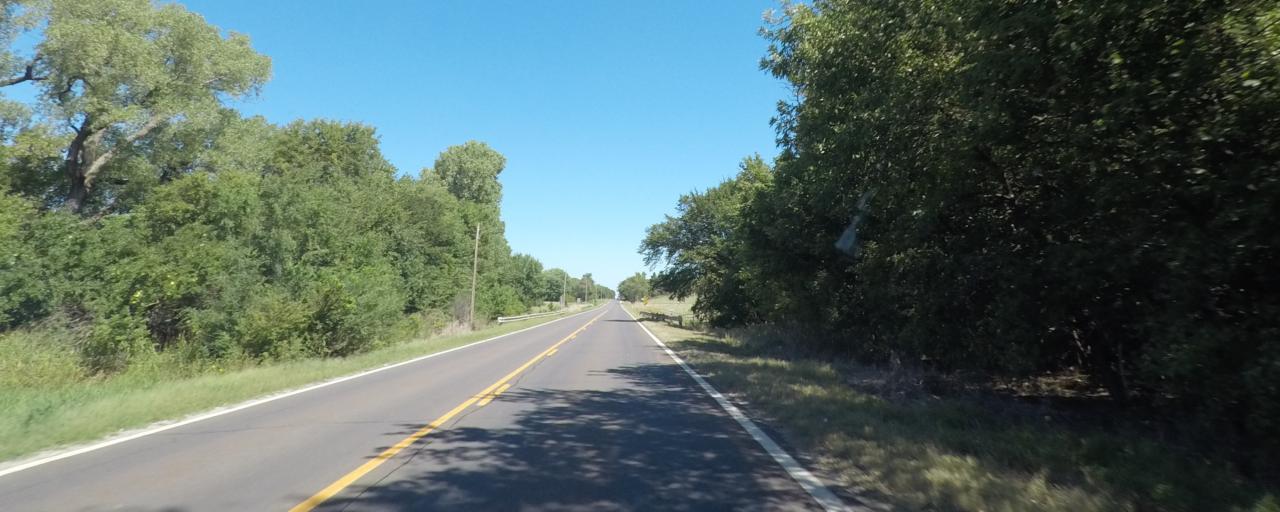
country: US
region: Kansas
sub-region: Sumner County
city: Wellington
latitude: 37.0672
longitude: -97.4013
